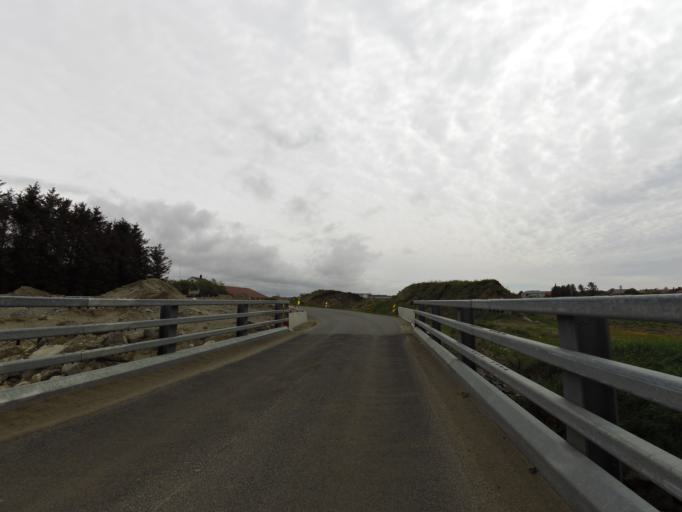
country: NO
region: Rogaland
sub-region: Ha
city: Naerbo
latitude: 58.6870
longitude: 5.5606
